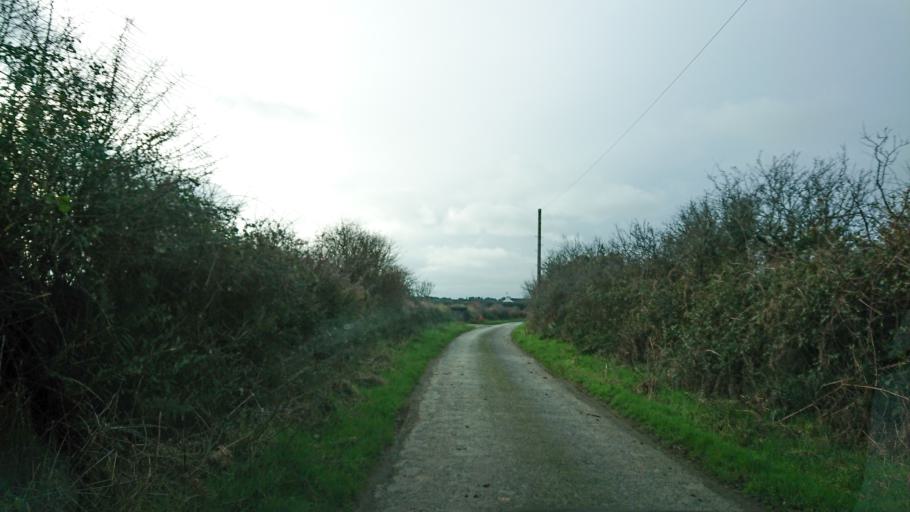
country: IE
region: Munster
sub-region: Waterford
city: Tra Mhor
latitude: 52.1962
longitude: -7.1699
